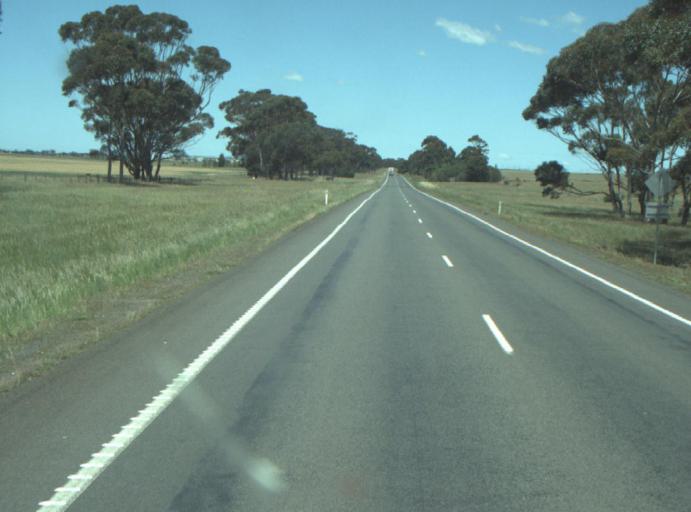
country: AU
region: Victoria
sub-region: Greater Geelong
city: Lara
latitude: -37.9416
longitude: 144.3572
